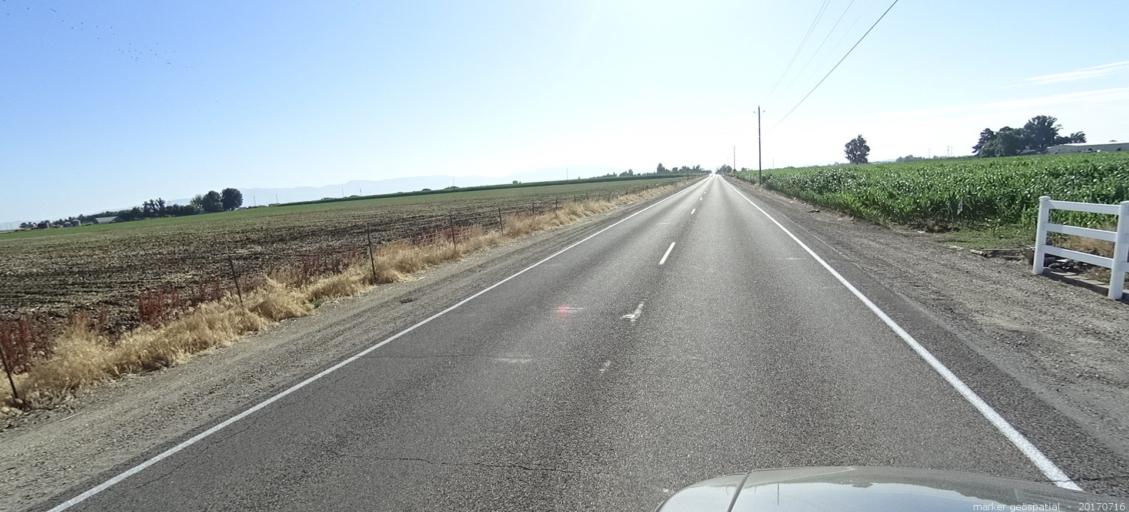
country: US
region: Idaho
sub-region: Ada County
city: Meridian
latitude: 43.5464
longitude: -116.3796
